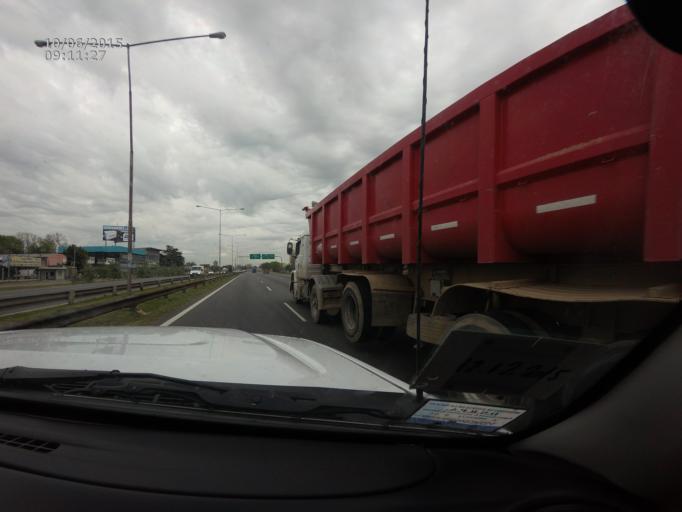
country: AR
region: Buenos Aires
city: Belen de Escobar
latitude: -34.3619
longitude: -58.7902
